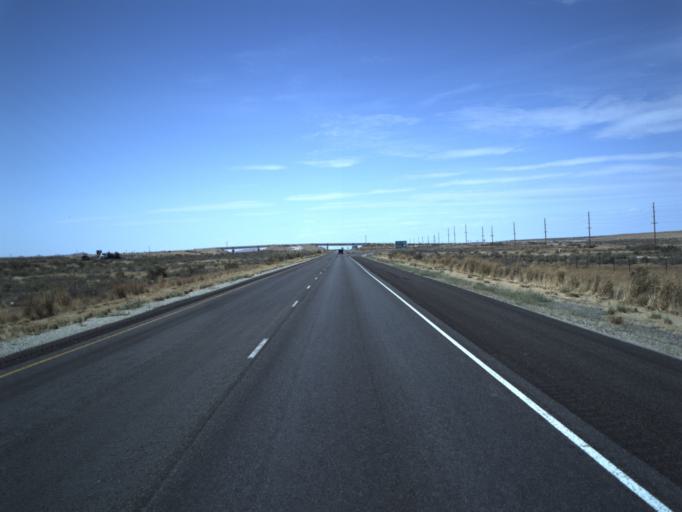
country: US
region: Utah
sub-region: Tooele County
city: Grantsville
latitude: 40.7352
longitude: -113.1040
